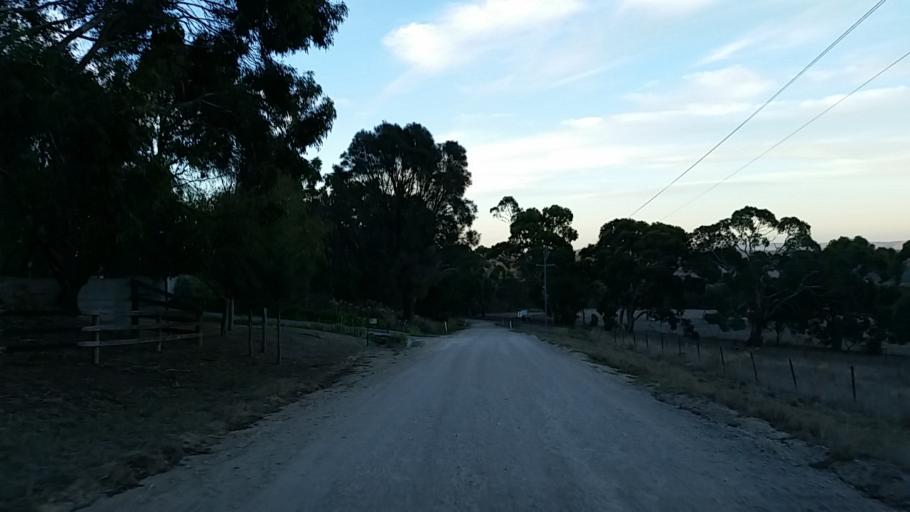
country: AU
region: South Australia
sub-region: Mount Barker
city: Nairne
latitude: -35.0612
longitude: 138.9246
